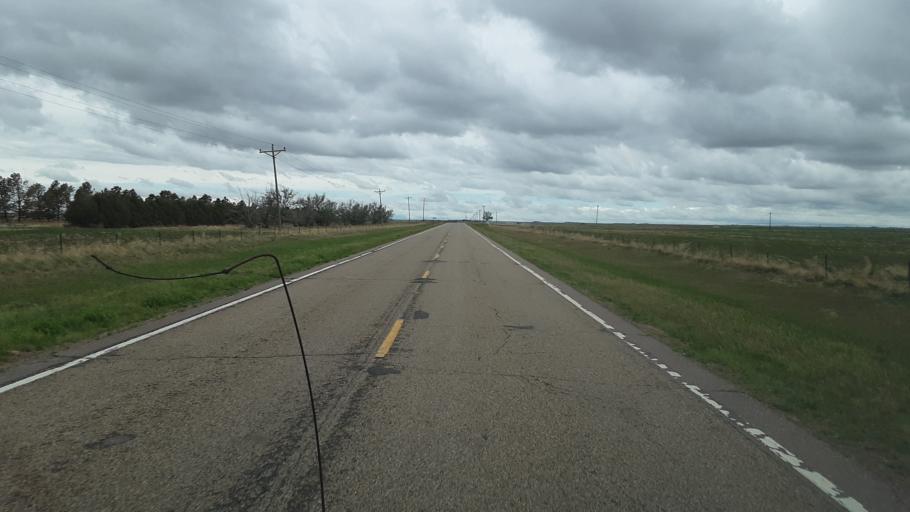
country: US
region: Colorado
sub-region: El Paso County
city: Ellicott
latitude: 38.8398
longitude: -103.9760
